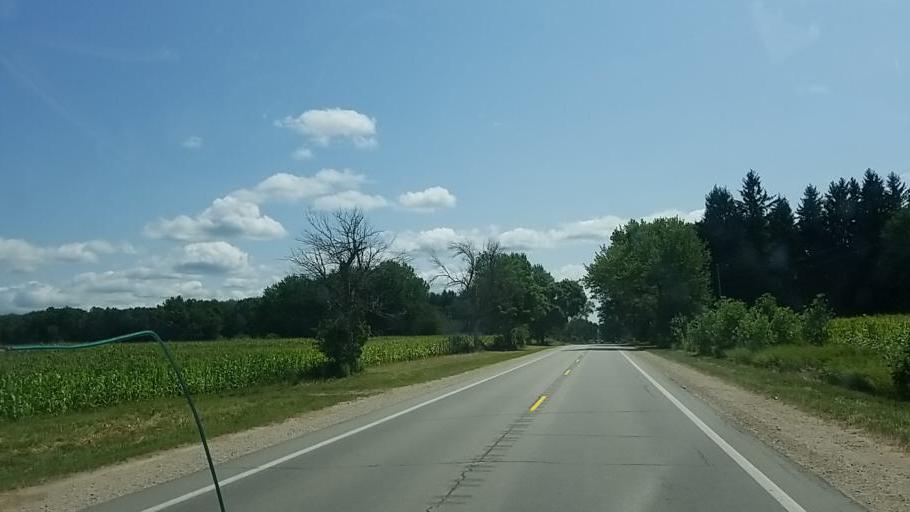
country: US
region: Michigan
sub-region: Newaygo County
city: Fremont
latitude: 43.4340
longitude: -85.9399
